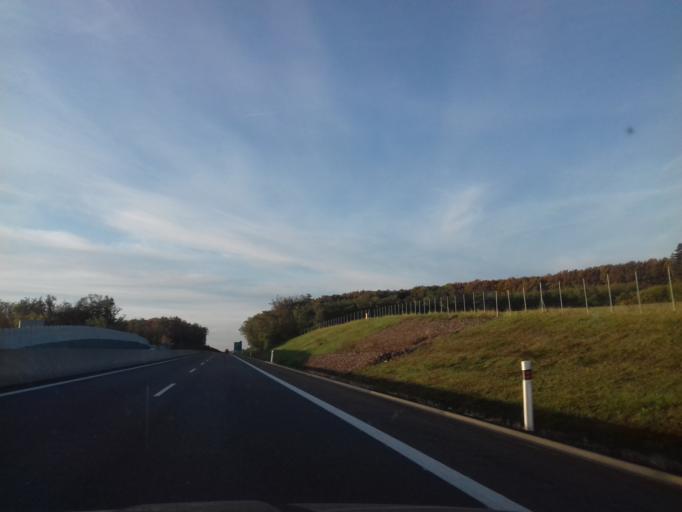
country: SK
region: Nitriansky
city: Tlmace
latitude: 48.3632
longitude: 18.4996
